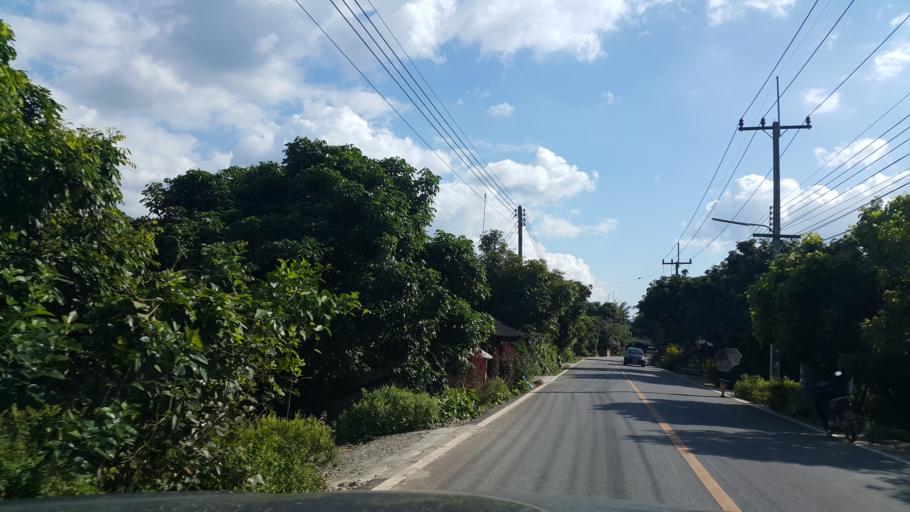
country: TH
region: Lamphun
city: Ban Thi
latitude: 18.5833
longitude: 99.2620
